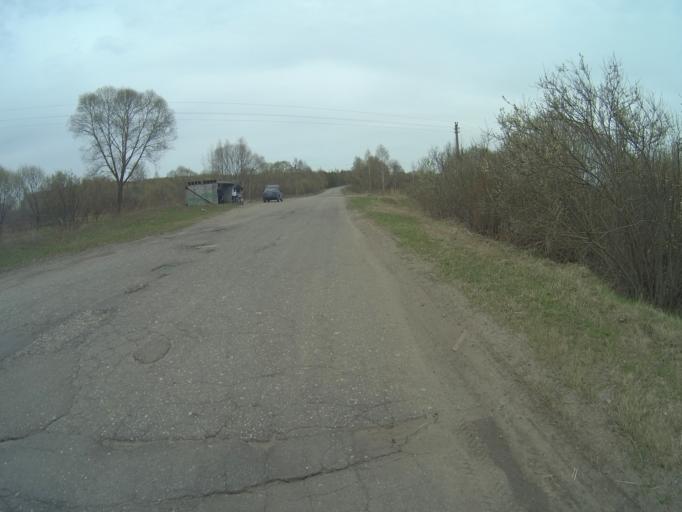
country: RU
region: Vladimir
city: Golovino
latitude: 55.9551
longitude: 40.6210
